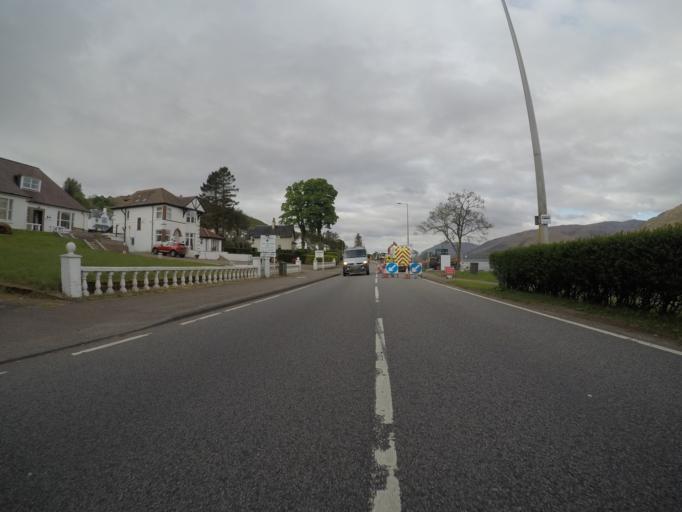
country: GB
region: Scotland
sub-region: Highland
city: Fort William
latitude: 56.8098
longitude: -5.1247
